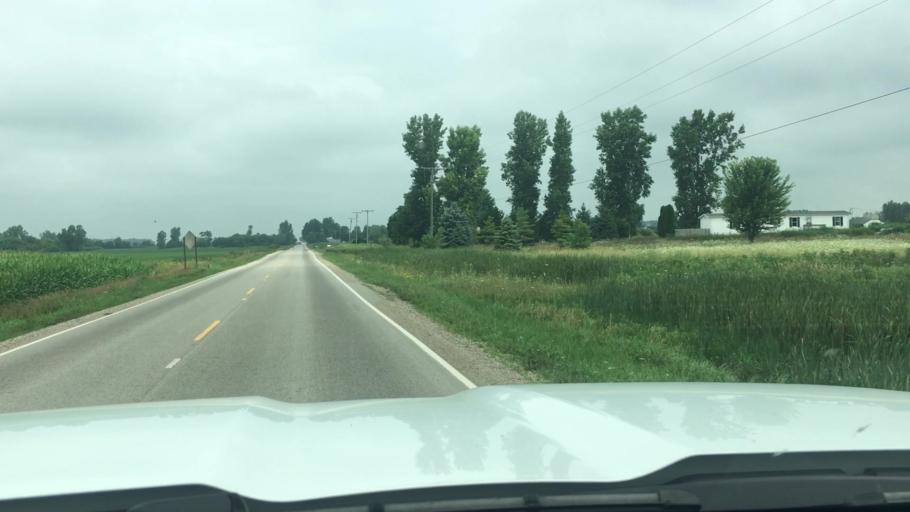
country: US
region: Michigan
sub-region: Sanilac County
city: Brown City
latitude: 43.2581
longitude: -82.9820
